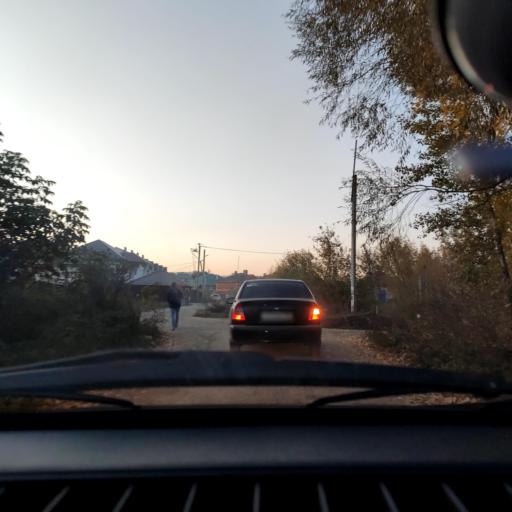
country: RU
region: Bashkortostan
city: Ufa
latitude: 54.6857
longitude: 55.9796
